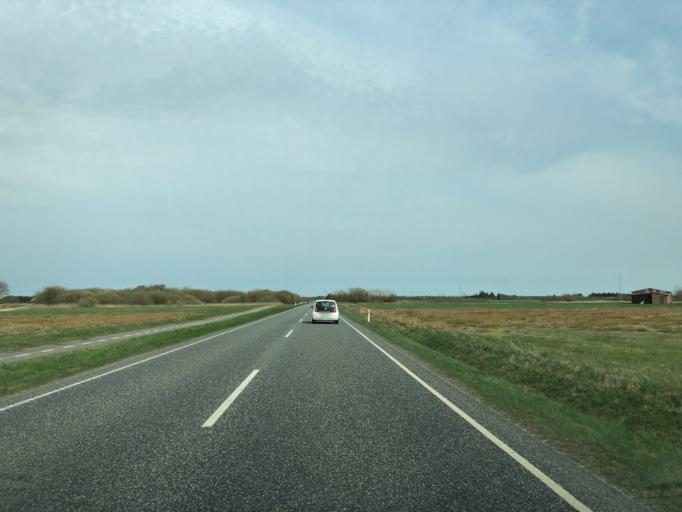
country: DK
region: Central Jutland
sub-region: Ringkobing-Skjern Kommune
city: Skjern
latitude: 55.8377
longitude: 8.3291
